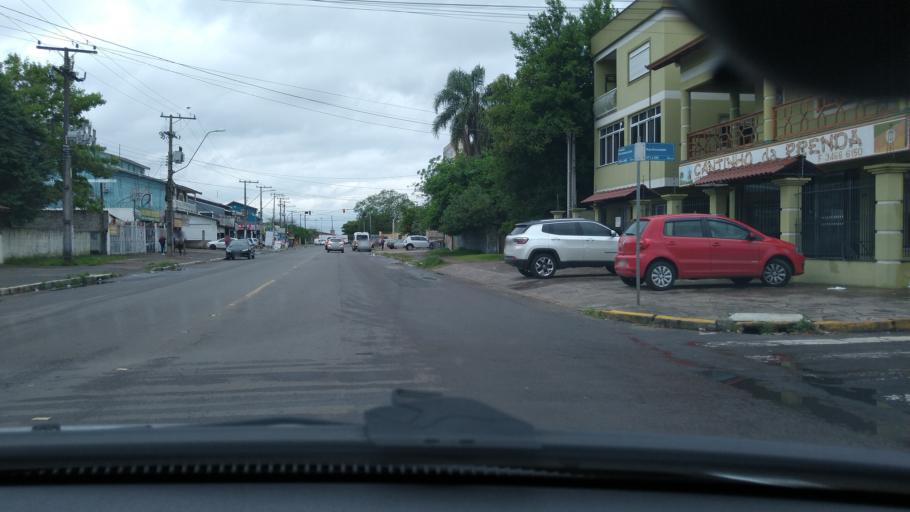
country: BR
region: Rio Grande do Sul
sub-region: Canoas
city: Canoas
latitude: -29.9018
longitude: -51.2082
